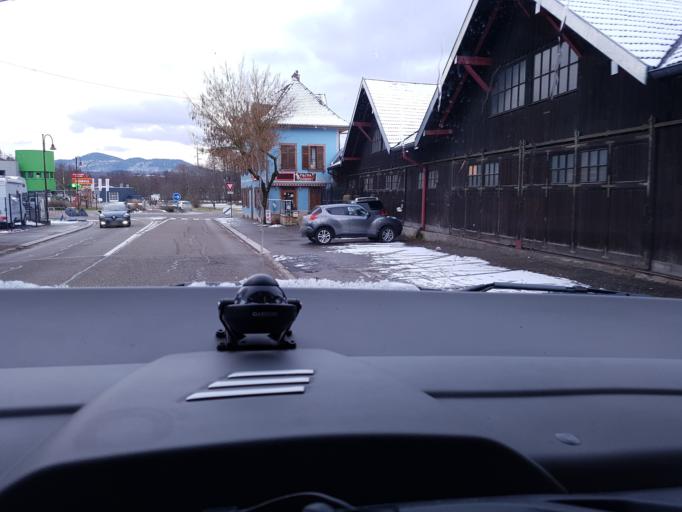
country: FR
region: Alsace
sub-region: Departement du Bas-Rhin
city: Ville
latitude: 48.3413
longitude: 7.3099
